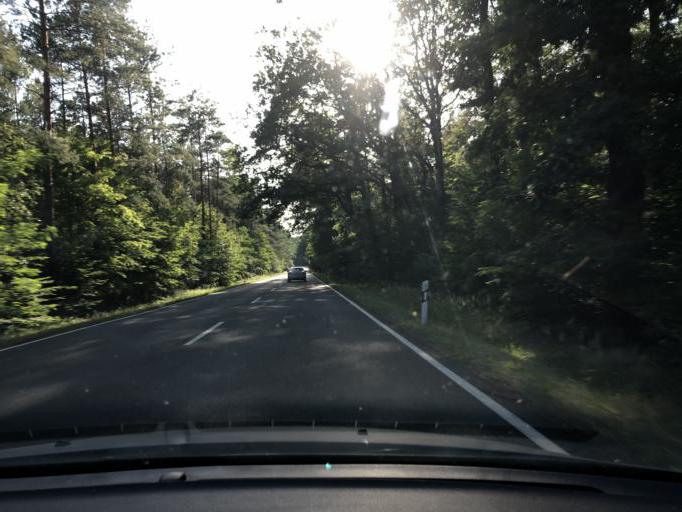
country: DE
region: Saxony
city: Wermsdorf
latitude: 51.3348
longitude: 12.9114
